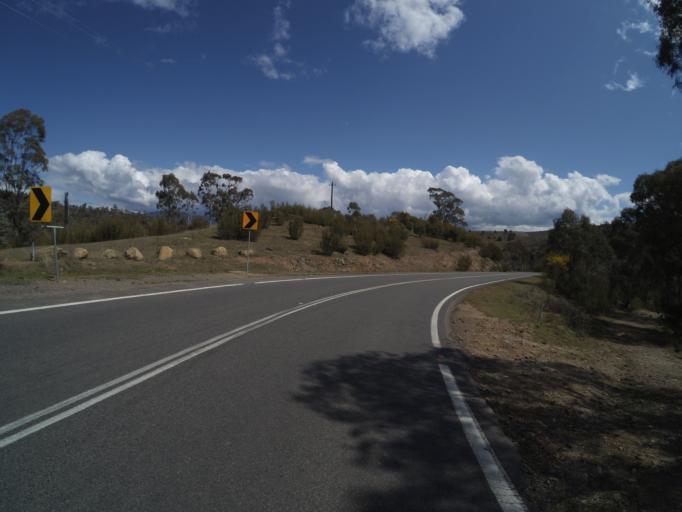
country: AU
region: Australian Capital Territory
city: Macquarie
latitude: -35.3238
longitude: 148.9441
